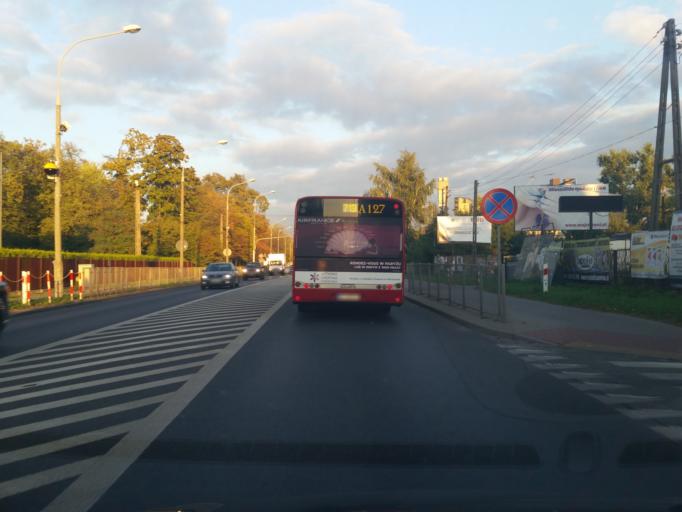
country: PL
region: Masovian Voivodeship
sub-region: Powiat warszawski zachodni
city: Ozarow Mazowiecki
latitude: 52.2104
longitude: 20.7947
